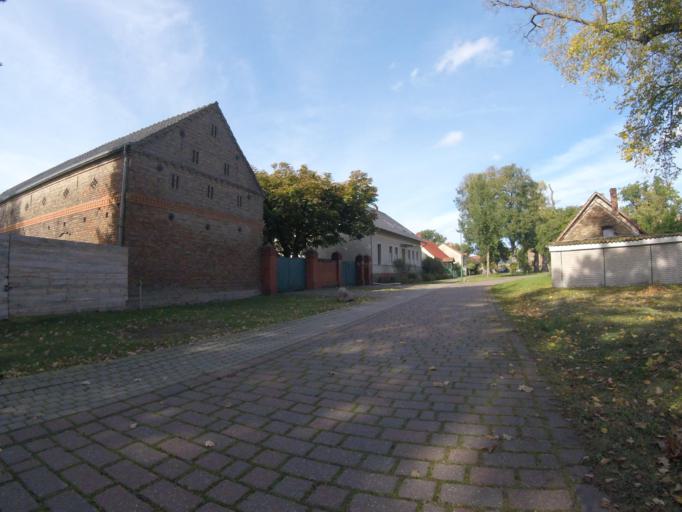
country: DE
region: Brandenburg
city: Bestensee
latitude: 52.2924
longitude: 13.7192
